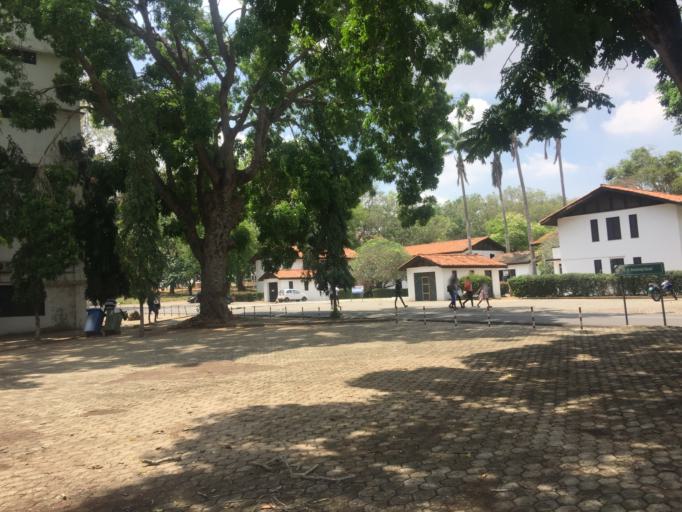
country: GH
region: Greater Accra
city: Medina Estates
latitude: 5.6481
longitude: -0.1880
